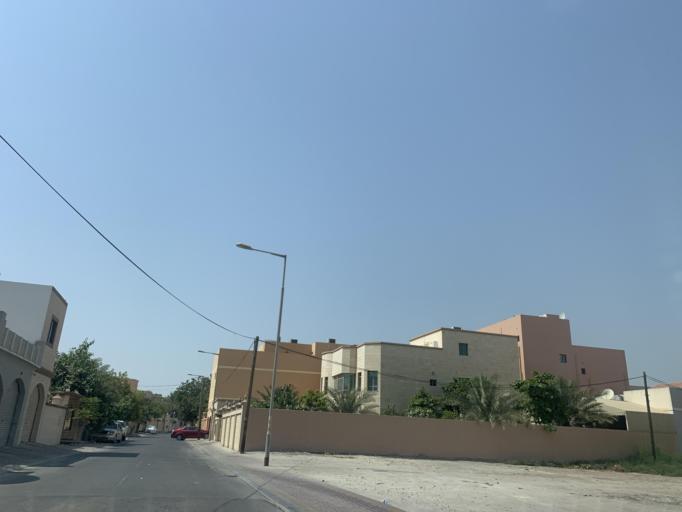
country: BH
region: Manama
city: Jidd Hafs
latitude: 26.2009
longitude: 50.5301
